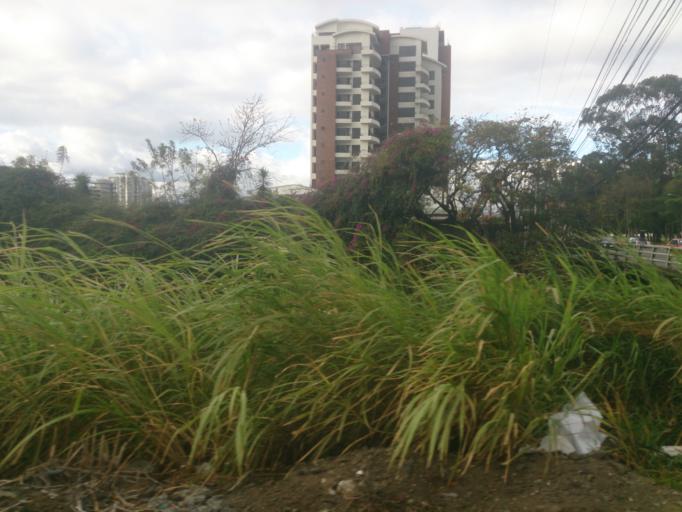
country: CR
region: San Jose
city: San Jose
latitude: 9.9337
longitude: -84.1106
